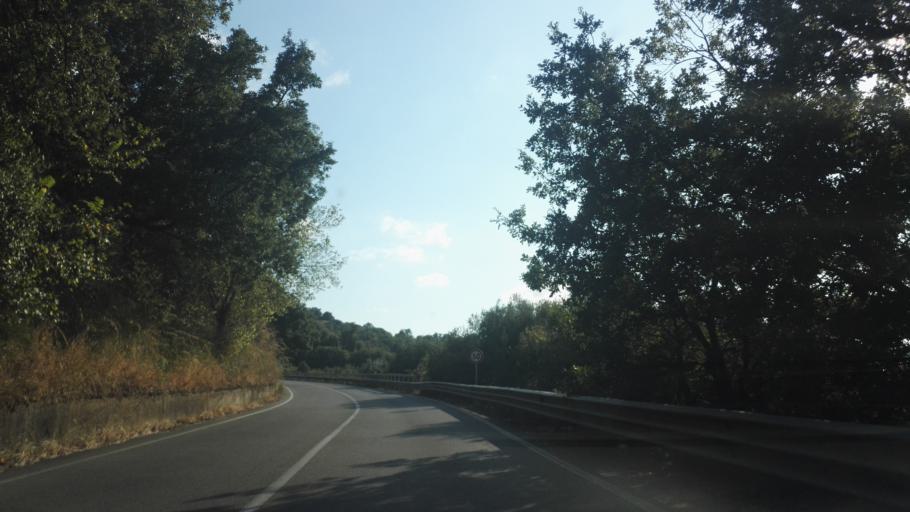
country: IT
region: Calabria
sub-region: Provincia di Vibo-Valentia
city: Stefanaconi
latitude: 38.7054
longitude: 16.1160
